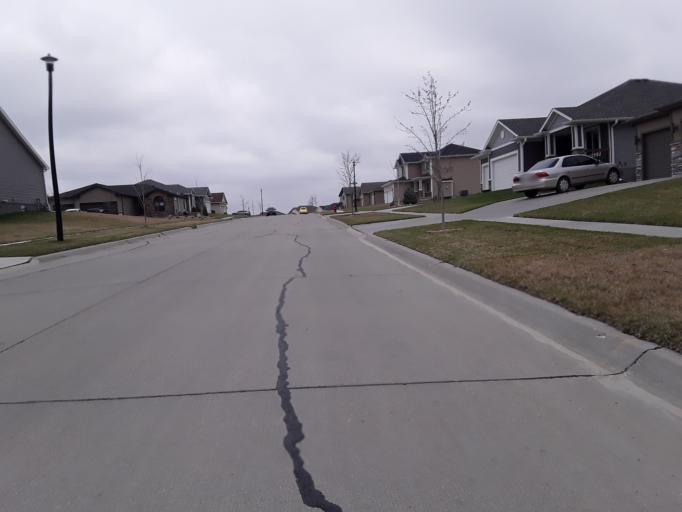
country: US
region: Nebraska
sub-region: Lancaster County
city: Lincoln
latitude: 40.8441
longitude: -96.5965
